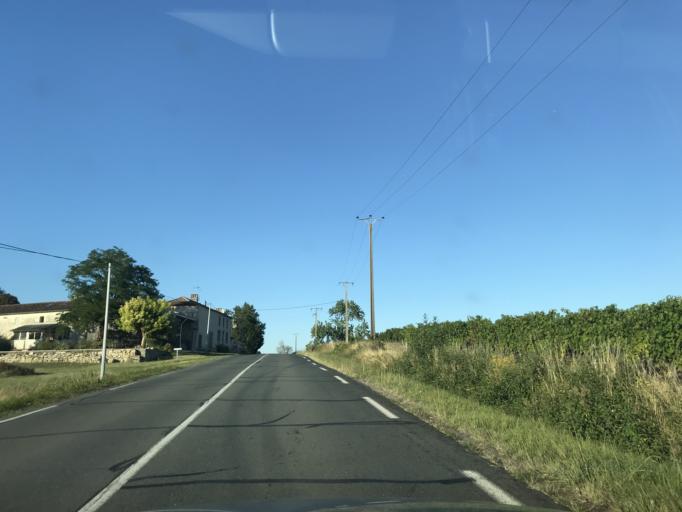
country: FR
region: Aquitaine
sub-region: Departement de la Gironde
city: Sauveterre-de-Guyenne
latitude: 44.6441
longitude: -0.1276
